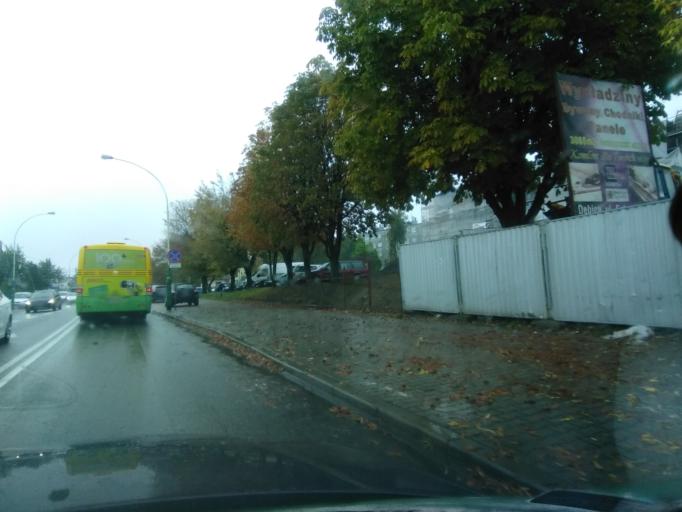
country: PL
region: Subcarpathian Voivodeship
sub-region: Powiat debicki
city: Debica
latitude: 50.0535
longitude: 21.4222
